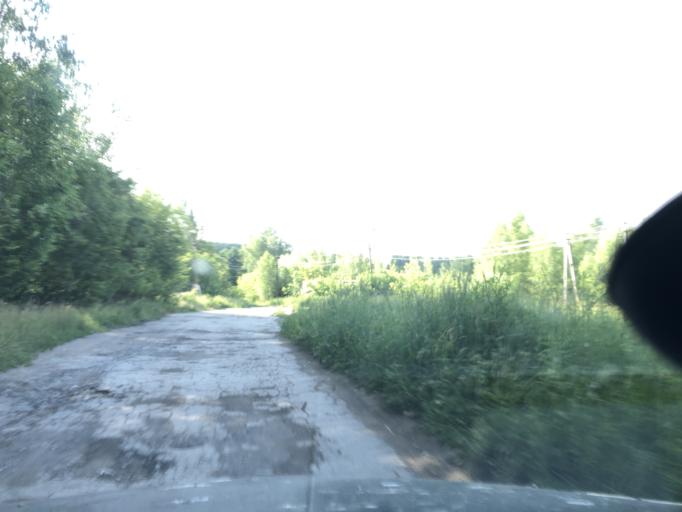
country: RU
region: Tula
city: Shvartsevskiy
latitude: 54.2528
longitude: 37.9268
